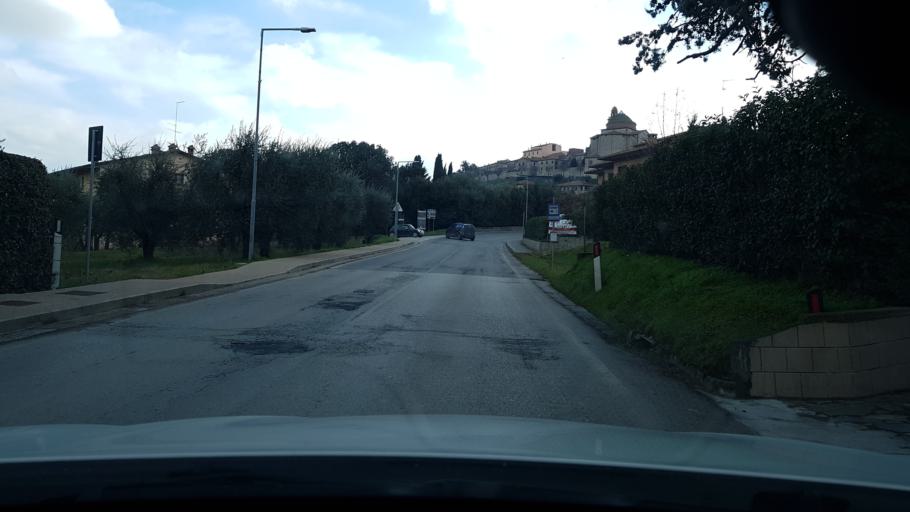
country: IT
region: Umbria
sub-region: Provincia di Perugia
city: Castiglione del Lago
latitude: 43.1286
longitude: 12.0462
